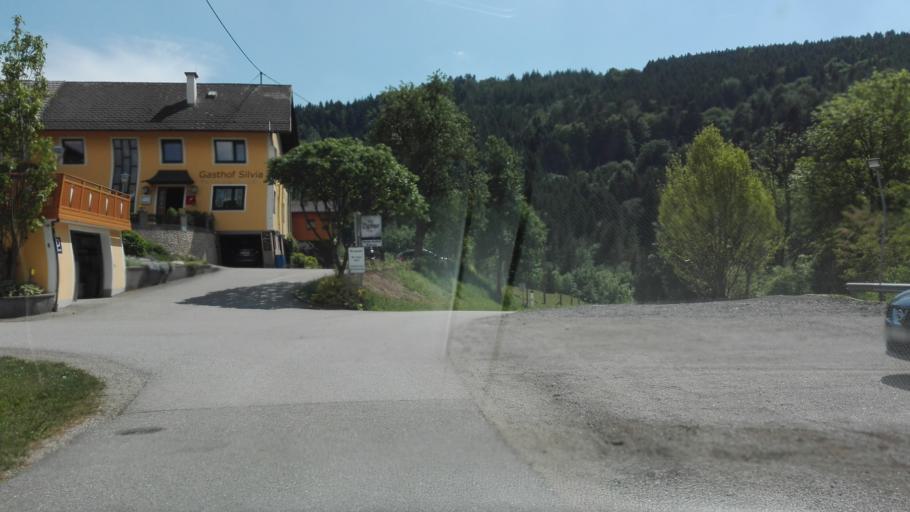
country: AT
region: Upper Austria
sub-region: Politischer Bezirk Rohrbach
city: Atzesberg
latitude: 48.4051
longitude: 13.8974
